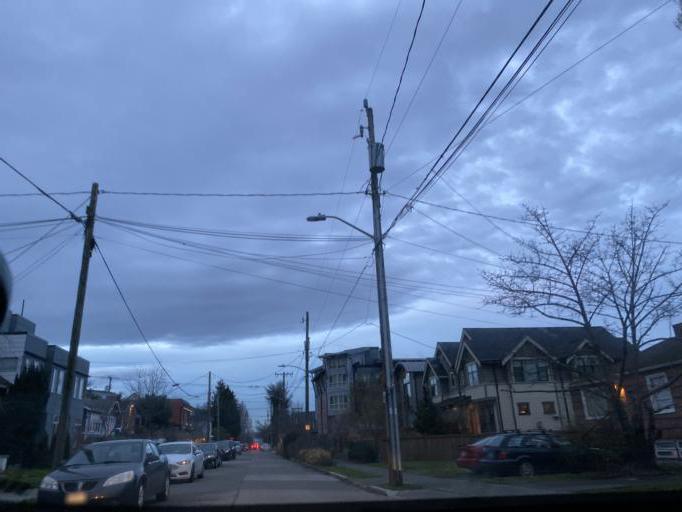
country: US
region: Washington
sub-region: King County
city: Seattle
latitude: 47.6475
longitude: -122.3833
